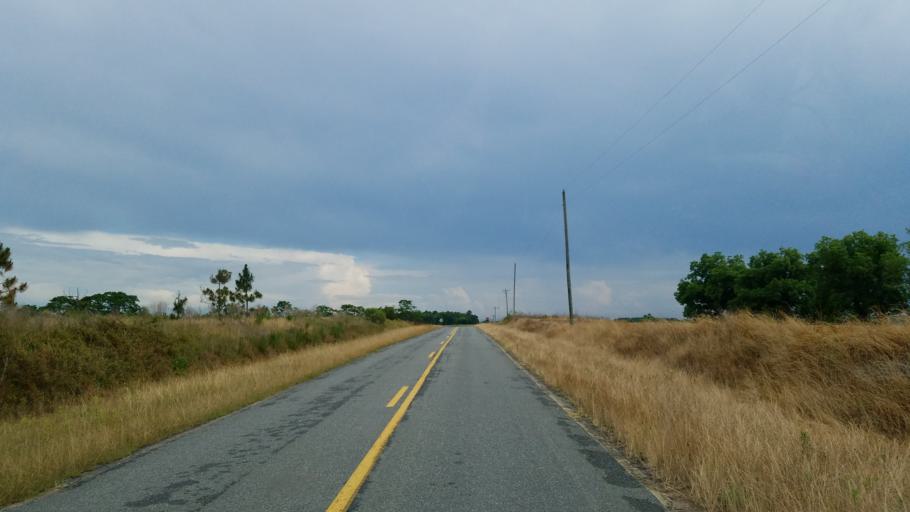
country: US
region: Georgia
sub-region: Dooly County
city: Unadilla
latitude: 32.2608
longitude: -83.7970
